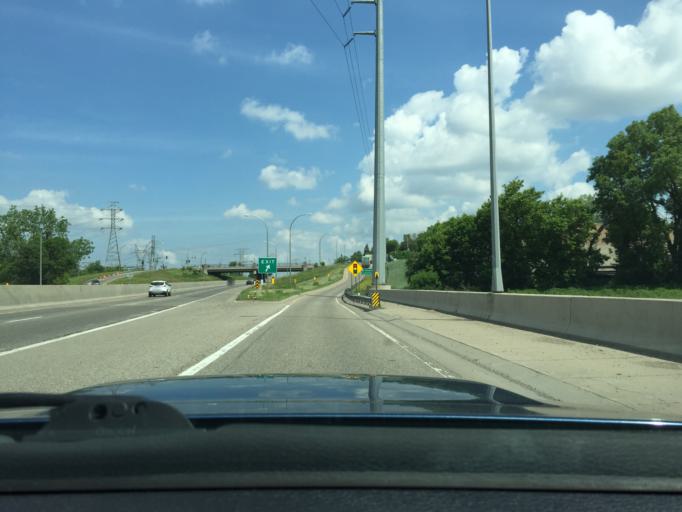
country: US
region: Minnesota
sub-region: Ramsey County
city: Lauderdale
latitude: 44.9890
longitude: -93.2038
